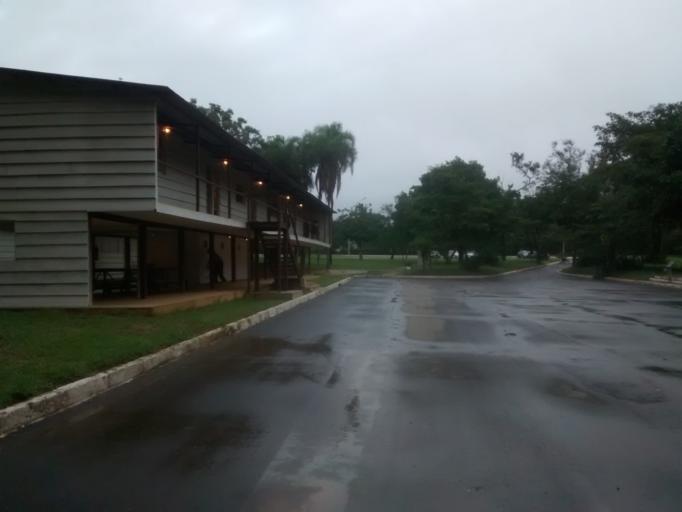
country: BR
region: Federal District
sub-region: Brasilia
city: Brasilia
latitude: -15.9478
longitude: -47.9882
